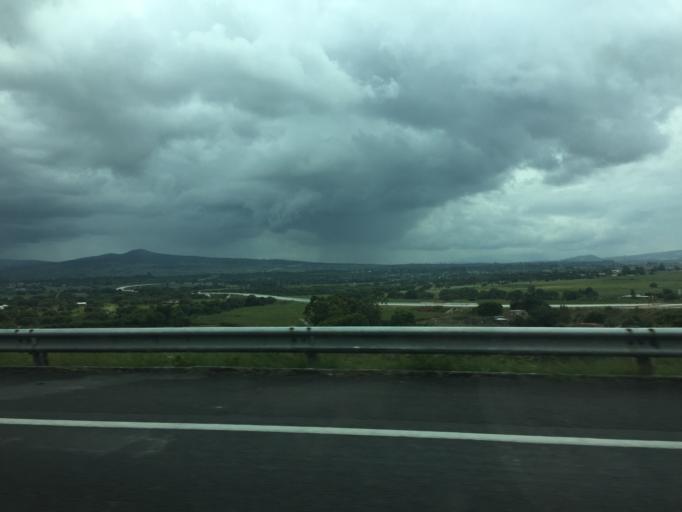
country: MX
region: Jalisco
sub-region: Zapotlanejo
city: La Mezquitera
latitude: 20.5843
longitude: -103.0972
